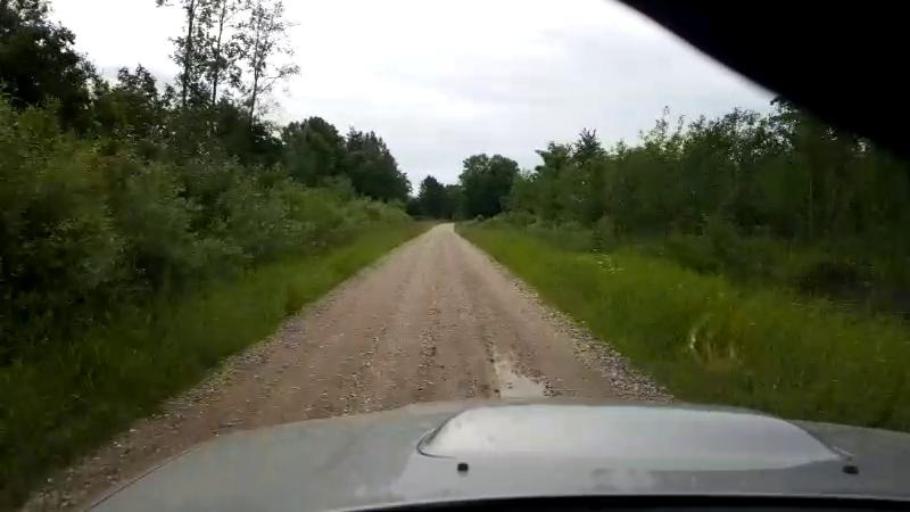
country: EE
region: Paernumaa
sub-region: Tootsi vald
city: Tootsi
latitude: 58.5512
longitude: 24.7449
